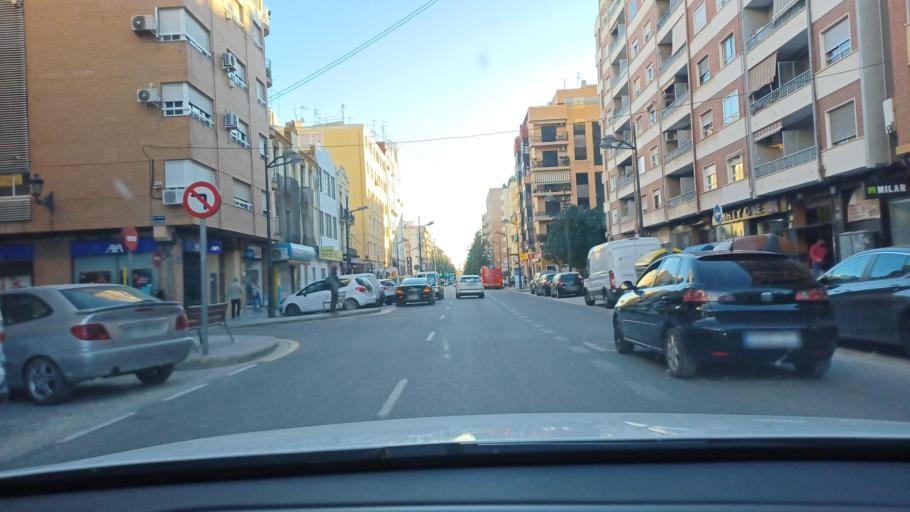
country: ES
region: Valencia
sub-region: Provincia de Valencia
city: Valencia
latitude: 39.4578
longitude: -0.3895
